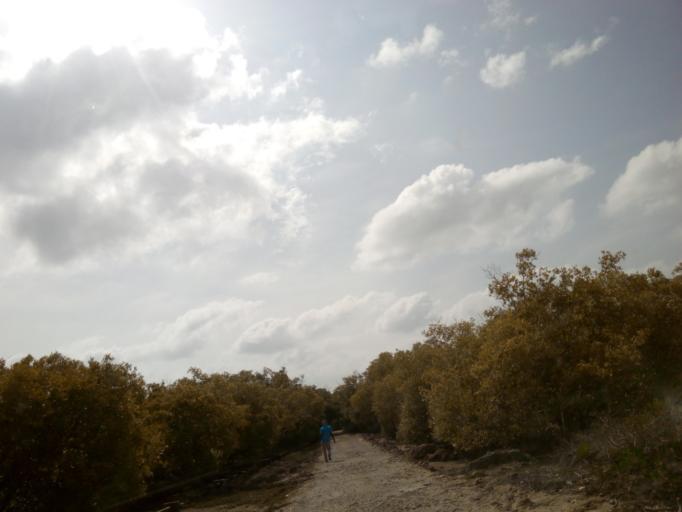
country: TZ
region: Zanzibar Central/South
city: Mahonda
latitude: -6.3112
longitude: 39.3797
